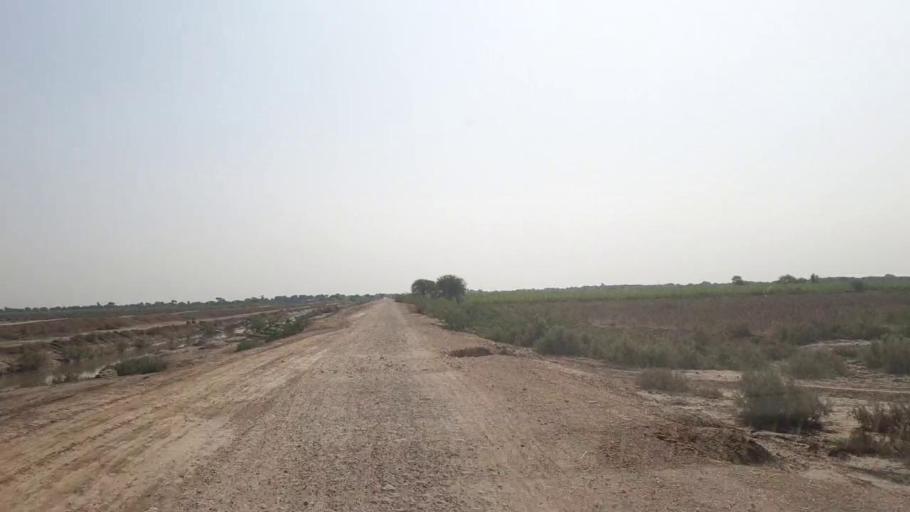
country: PK
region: Sindh
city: Kadhan
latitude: 24.4721
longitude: 68.9036
